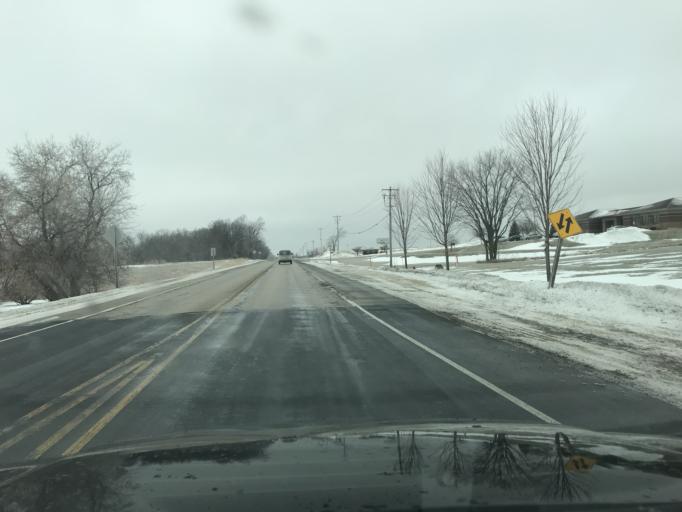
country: US
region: Wisconsin
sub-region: Dane County
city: Cottage Grove
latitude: 43.0895
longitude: -89.2236
